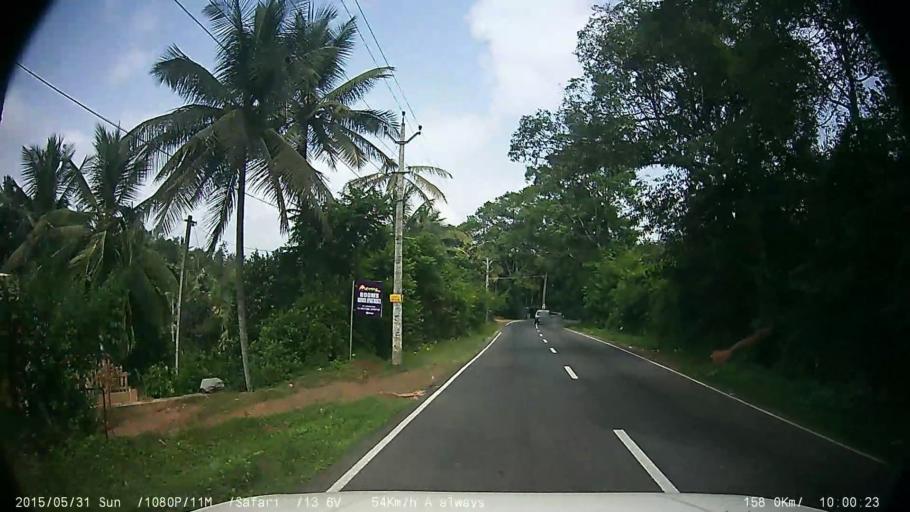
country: IN
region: Kerala
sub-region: Wayanad
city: Kalpetta
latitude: 11.5847
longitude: 76.0659
